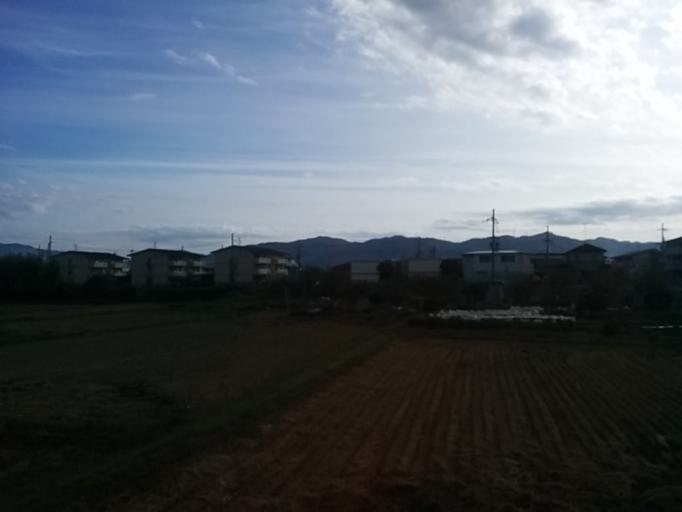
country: JP
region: Kyoto
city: Tanabe
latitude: 34.8096
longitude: 135.7776
